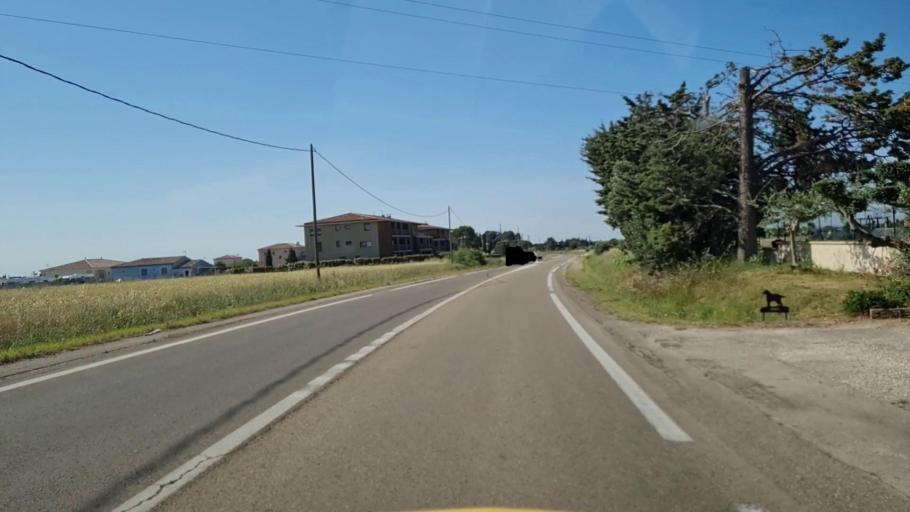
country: FR
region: Languedoc-Roussillon
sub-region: Departement du Gard
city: Saint-Gilles
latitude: 43.6996
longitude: 4.4245
